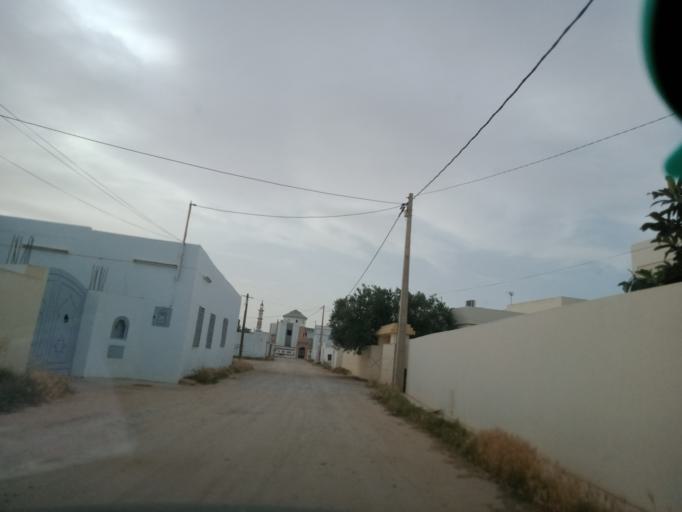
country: TN
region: Safaqis
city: Al Qarmadah
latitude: 34.8041
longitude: 10.7538
